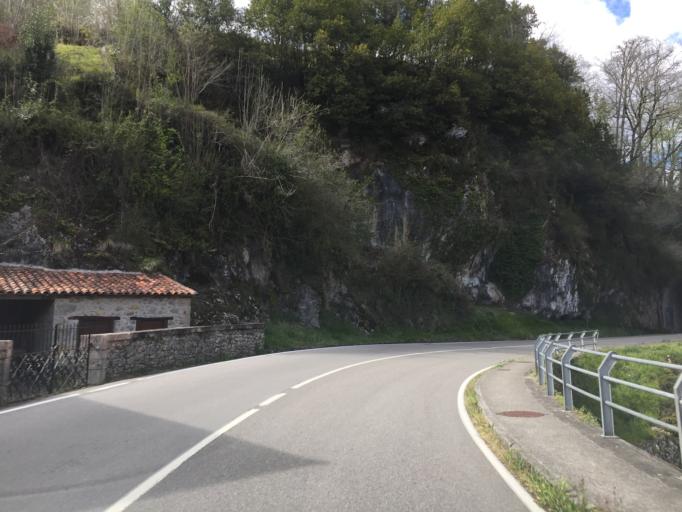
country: ES
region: Asturias
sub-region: Province of Asturias
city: Cangas de Onis
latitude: 43.3250
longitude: -5.0790
